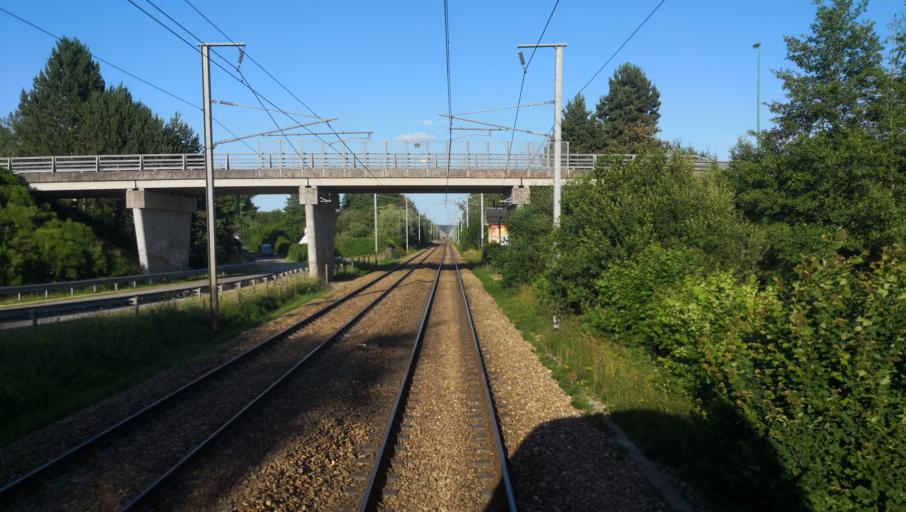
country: FR
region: Haute-Normandie
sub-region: Departement de l'Eure
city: Saint-Sebastien-de-Morsent
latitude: 48.9944
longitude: 1.0557
